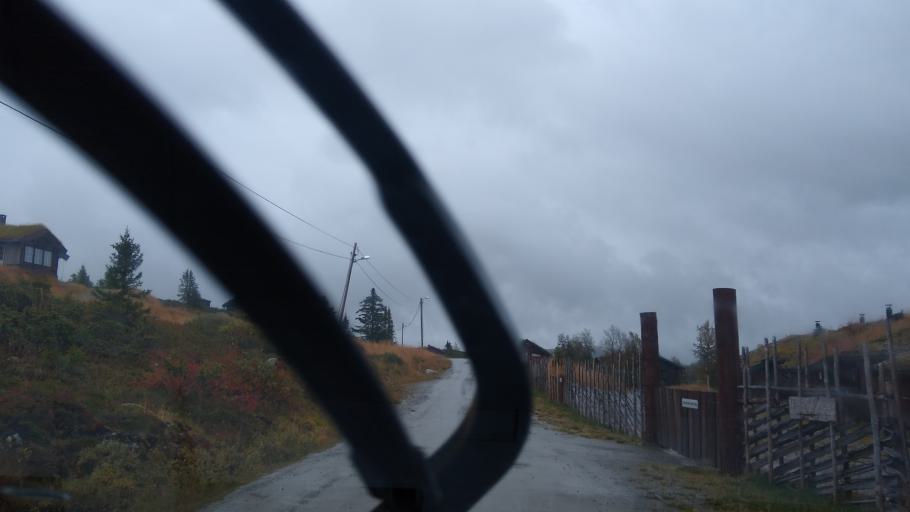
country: NO
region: Oppland
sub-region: Ringebu
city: Ringebu
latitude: 61.6725
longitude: 10.0952
